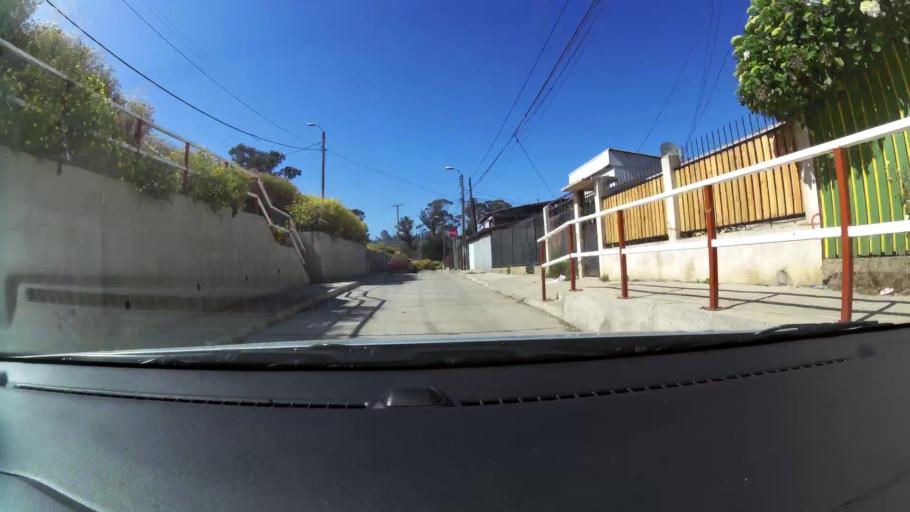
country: CL
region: Valparaiso
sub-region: Provincia de Valparaiso
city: Valparaiso
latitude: -33.0533
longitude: -71.6483
